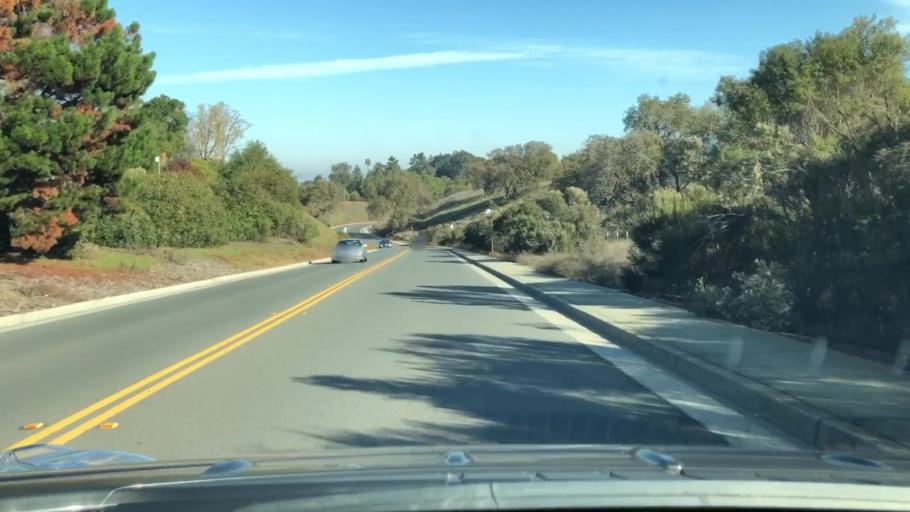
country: US
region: California
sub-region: Santa Clara County
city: Loyola
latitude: 37.3313
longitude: -122.0799
